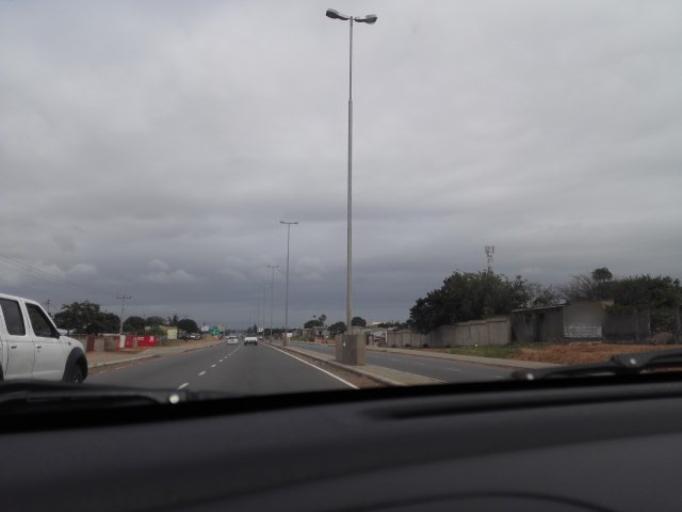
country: MZ
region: Maputo City
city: Maputo
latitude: -25.8230
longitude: 32.5904
